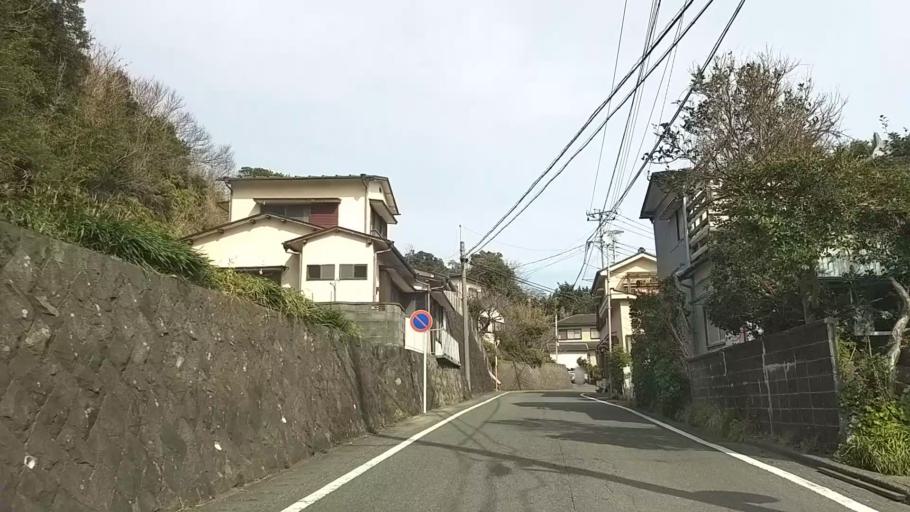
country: JP
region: Shizuoka
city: Shimoda
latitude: 34.6625
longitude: 138.9643
